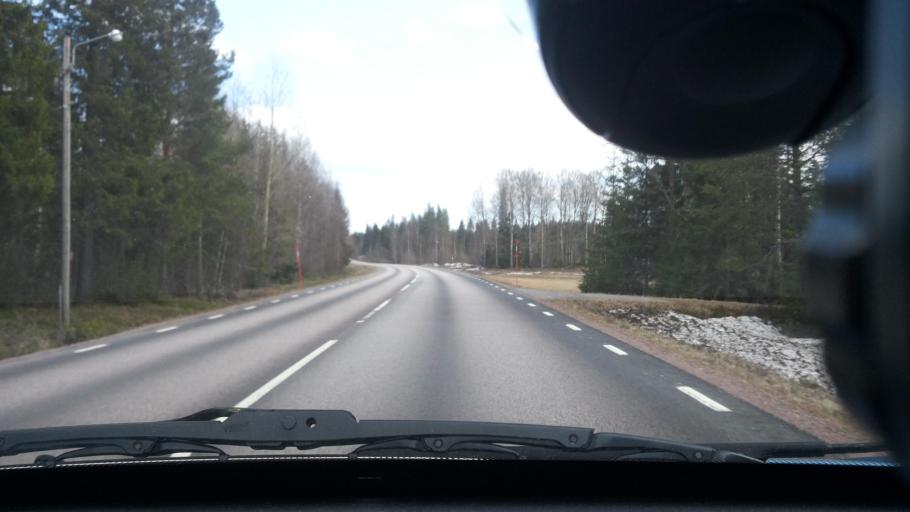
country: SE
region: Norrbotten
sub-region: Lulea Kommun
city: Gammelstad
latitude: 65.6065
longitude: 21.9641
